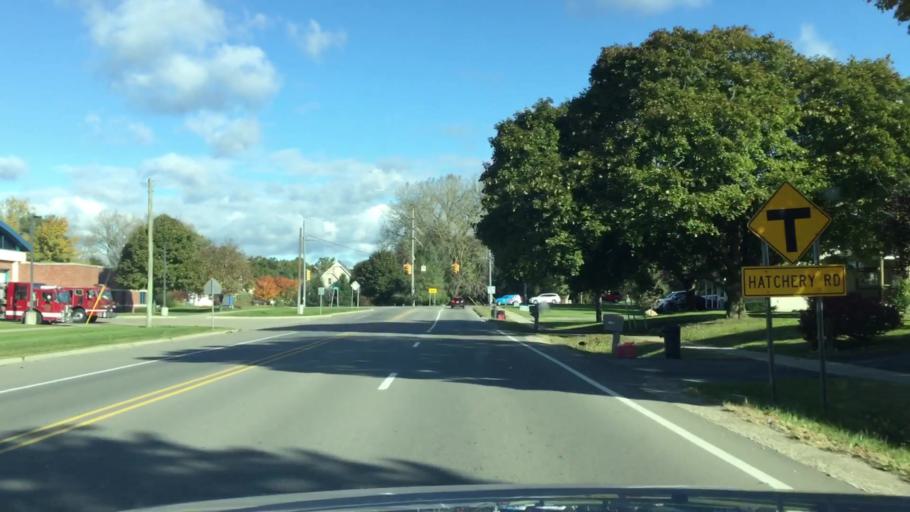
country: US
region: Michigan
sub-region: Oakland County
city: Waterford
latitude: 42.6737
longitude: -83.3868
